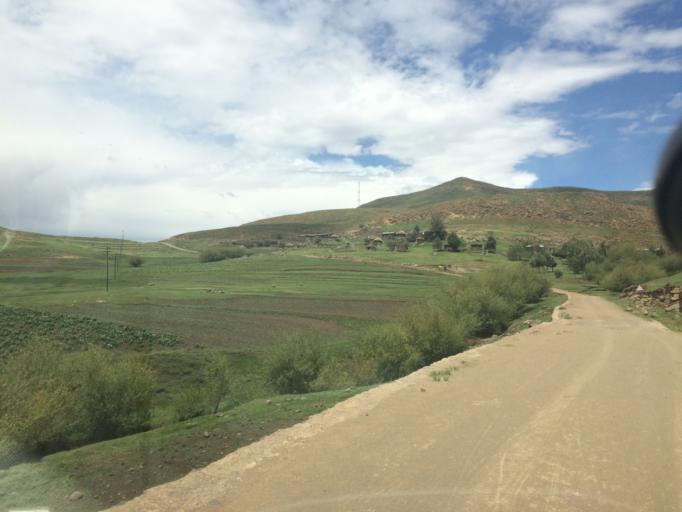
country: LS
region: Maseru
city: Nako
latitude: -29.8633
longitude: 28.0383
